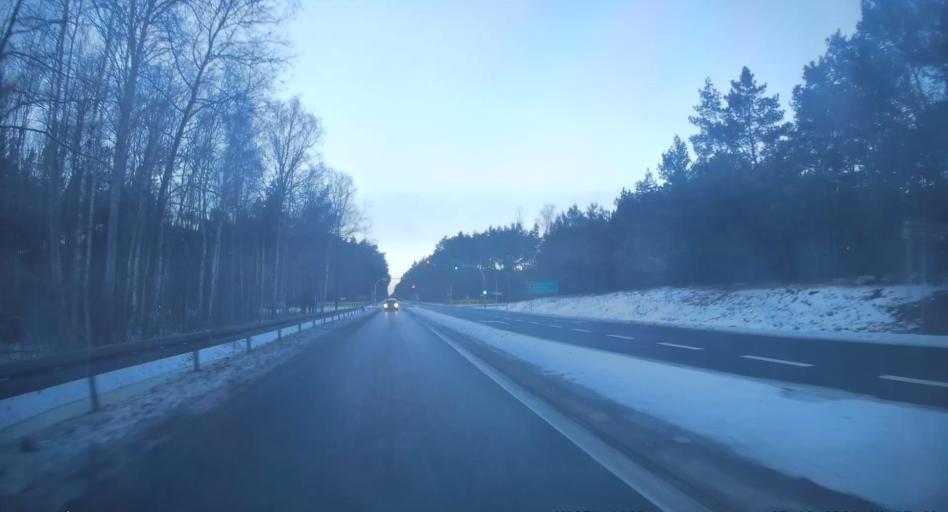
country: PL
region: Swietokrzyskie
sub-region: Powiat konecki
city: Ruda Maleniecka
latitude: 51.1439
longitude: 20.2449
